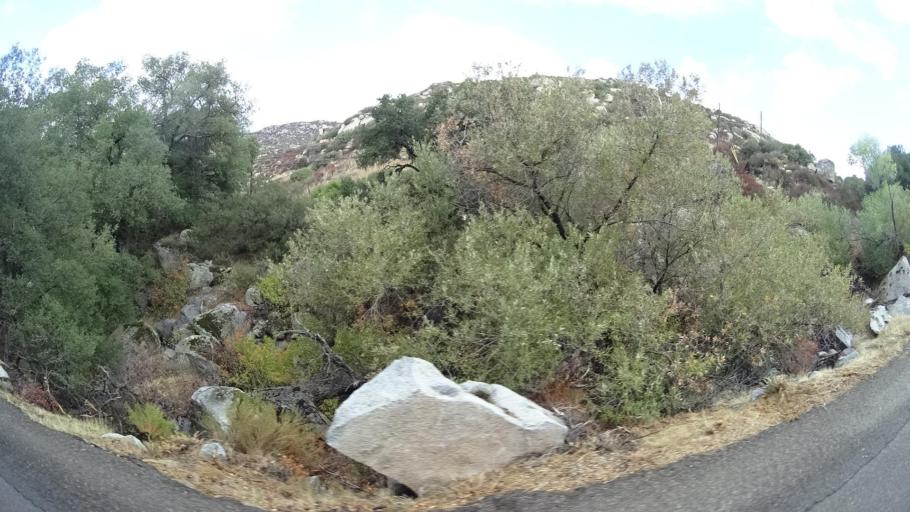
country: US
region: California
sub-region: San Diego County
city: Campo
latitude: 32.6072
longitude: -116.4771
